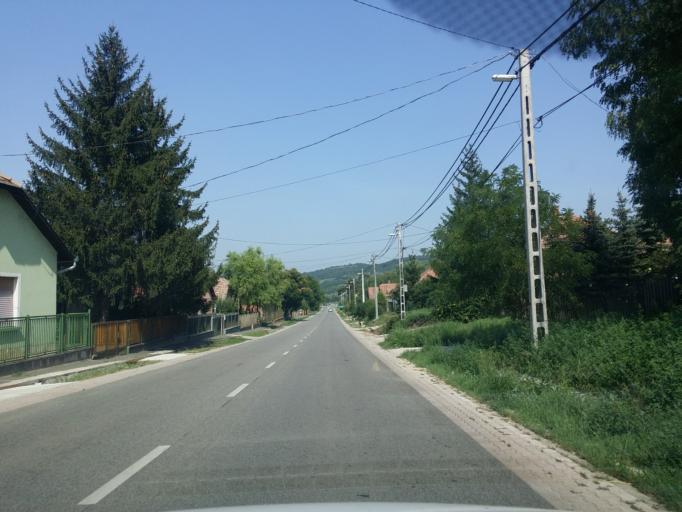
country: HU
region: Tolna
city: Pincehely
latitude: 46.6909
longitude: 18.4524
